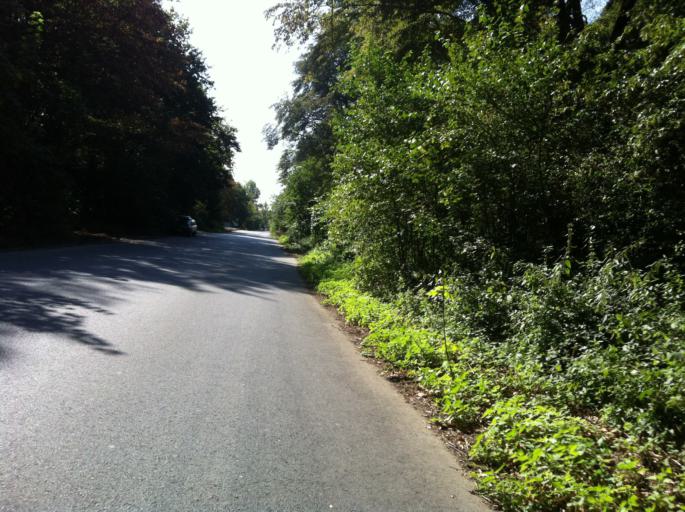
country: DE
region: North Rhine-Westphalia
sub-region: Regierungsbezirk Koln
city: Hoehenberg
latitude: 50.9174
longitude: 7.0229
